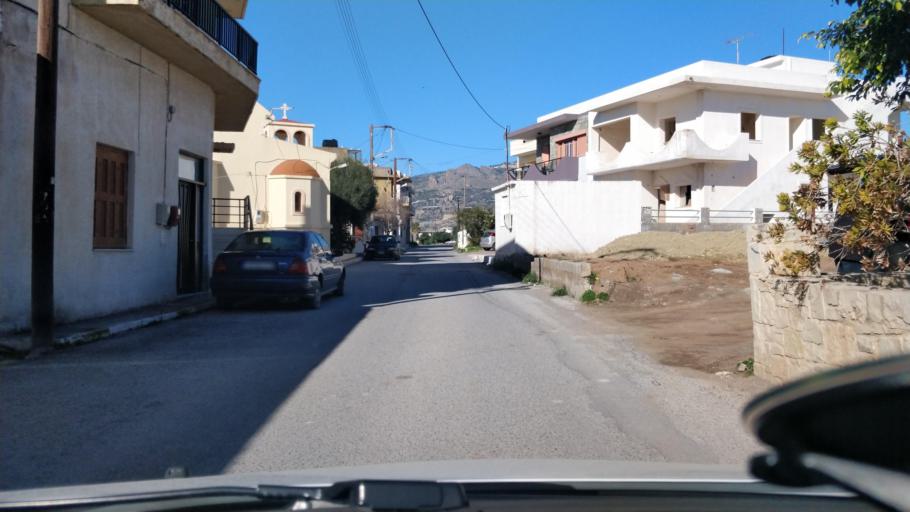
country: GR
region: Crete
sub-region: Nomos Lasithiou
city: Gra Liyia
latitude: 35.0164
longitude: 25.6903
